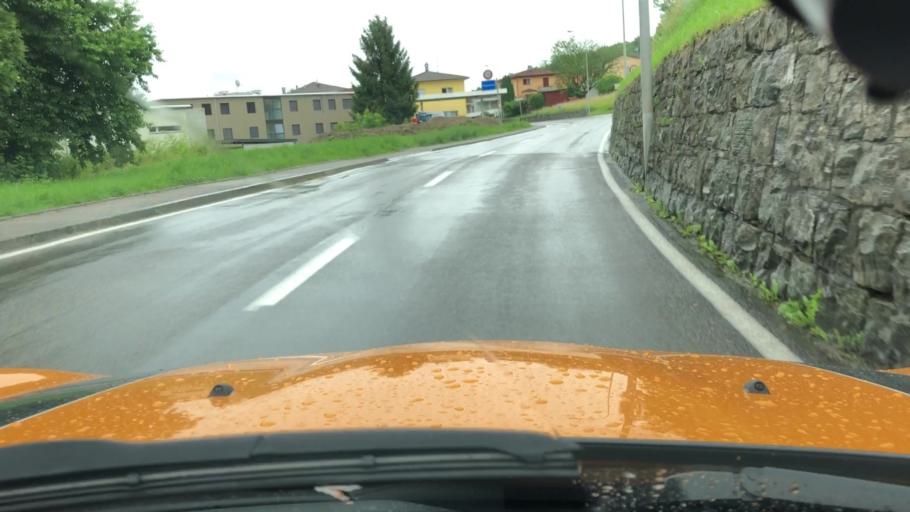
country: CH
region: Ticino
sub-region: Mendrisio District
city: Novazzano
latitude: 45.8444
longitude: 8.9716
